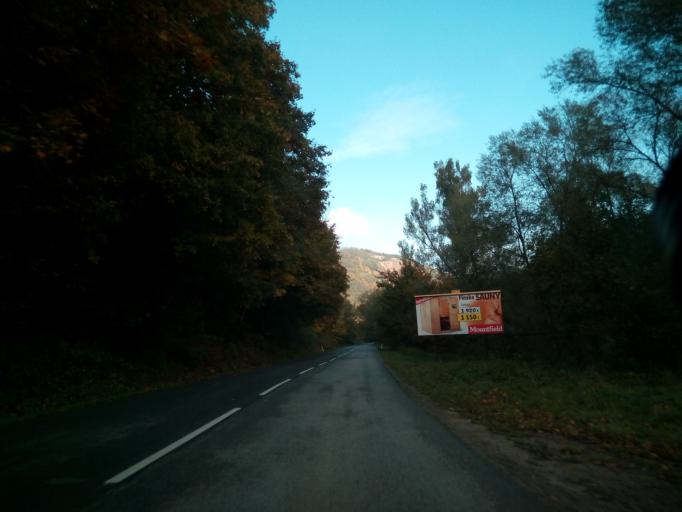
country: SK
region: Kosicky
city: Gelnica
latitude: 48.8695
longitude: 21.0037
